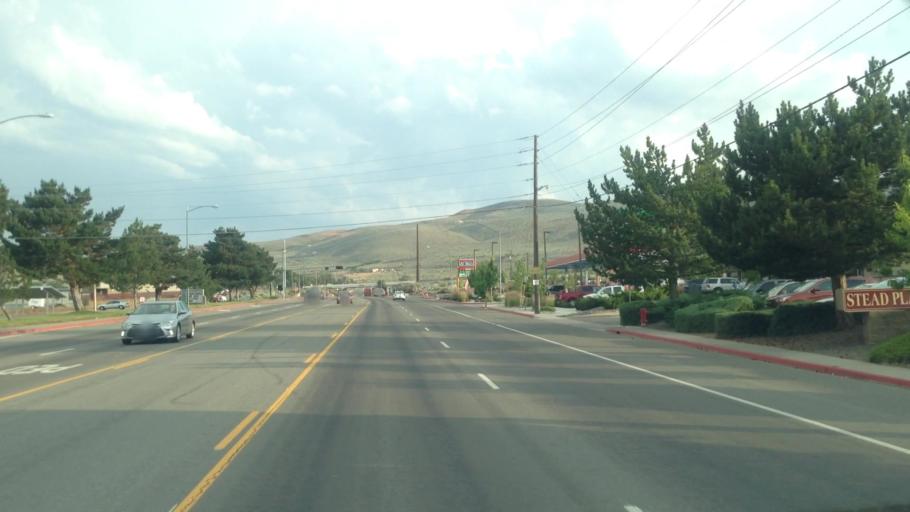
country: US
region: Nevada
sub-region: Washoe County
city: Lemmon Valley
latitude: 39.6234
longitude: -119.8822
